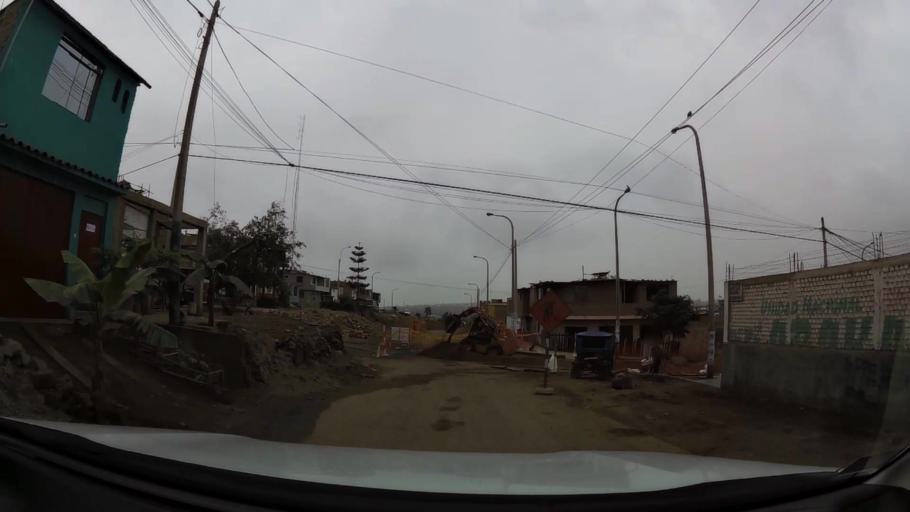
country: PE
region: Lima
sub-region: Lima
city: Punta Hermosa
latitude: -12.2369
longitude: -76.9074
